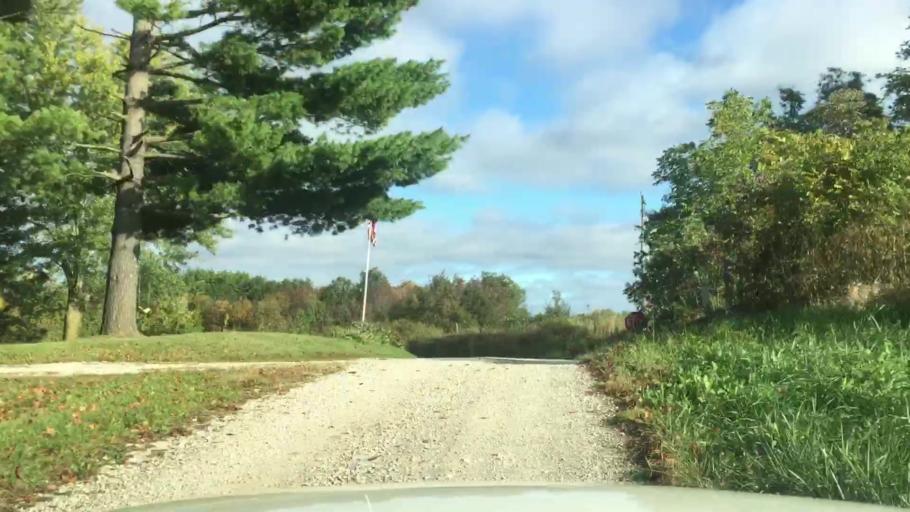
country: US
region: Missouri
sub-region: Howard County
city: New Franklin
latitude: 39.1048
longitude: -92.7792
